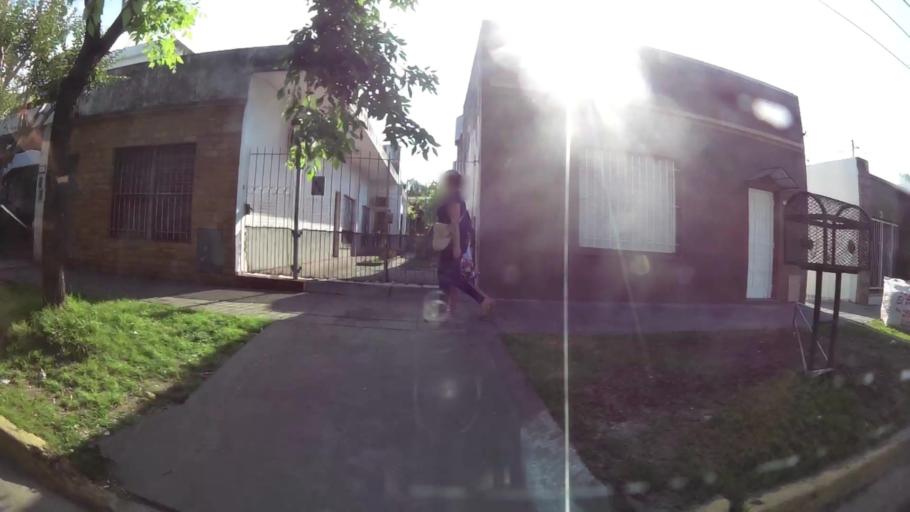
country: AR
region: Buenos Aires
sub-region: Partido de Merlo
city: Merlo
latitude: -34.6670
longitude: -58.7220
